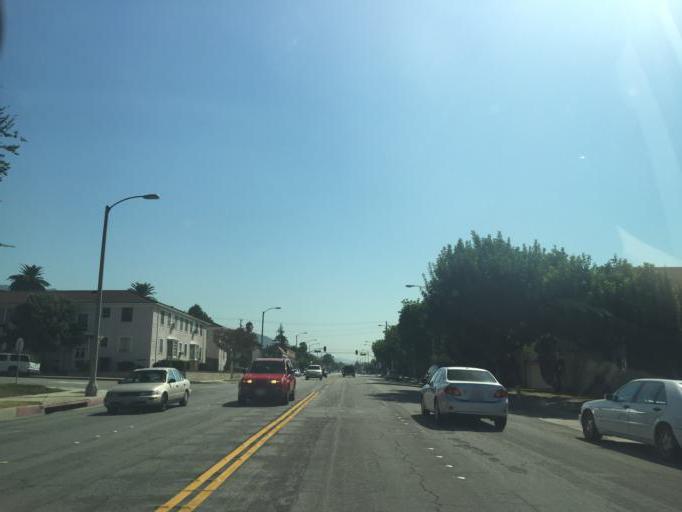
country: US
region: California
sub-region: Los Angeles County
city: Monrovia
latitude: 34.1512
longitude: -118.0117
